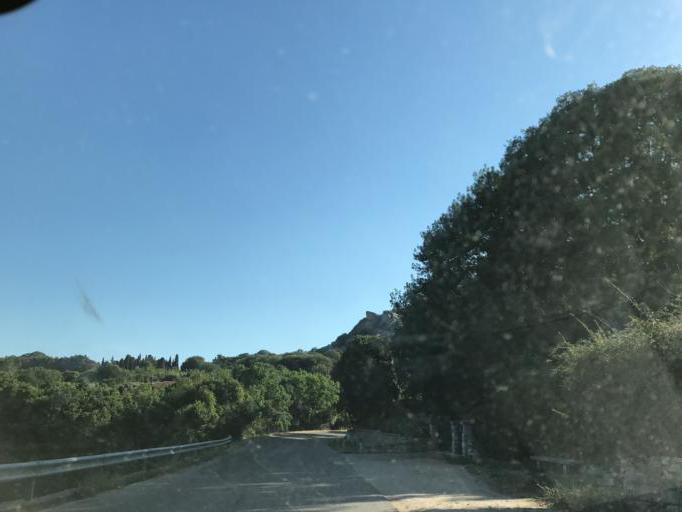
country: IT
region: Sardinia
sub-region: Provincia di Olbia-Tempio
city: Aggius
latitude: 40.9368
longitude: 9.0681
